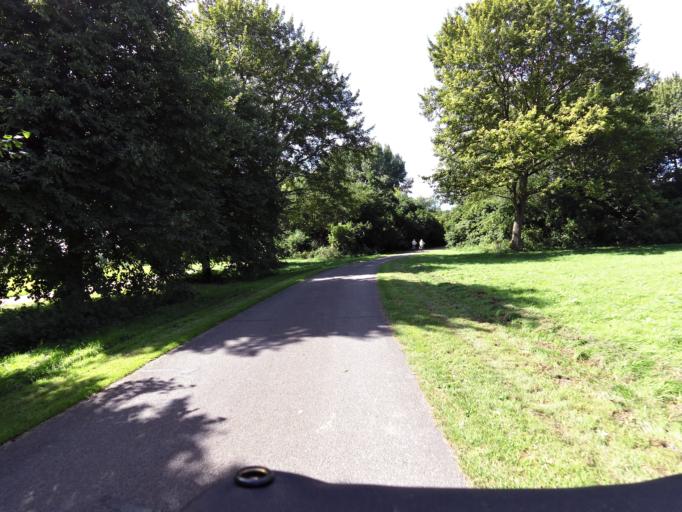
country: NL
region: South Holland
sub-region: Gemeente Zwijndrecht
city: Heerjansdam
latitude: 51.8112
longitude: 4.5766
